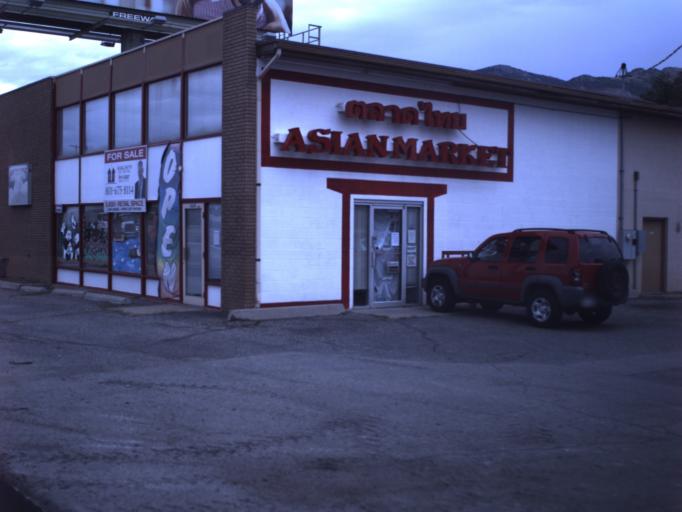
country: US
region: Utah
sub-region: Weber County
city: Ogden
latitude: 41.2412
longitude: -111.9783
